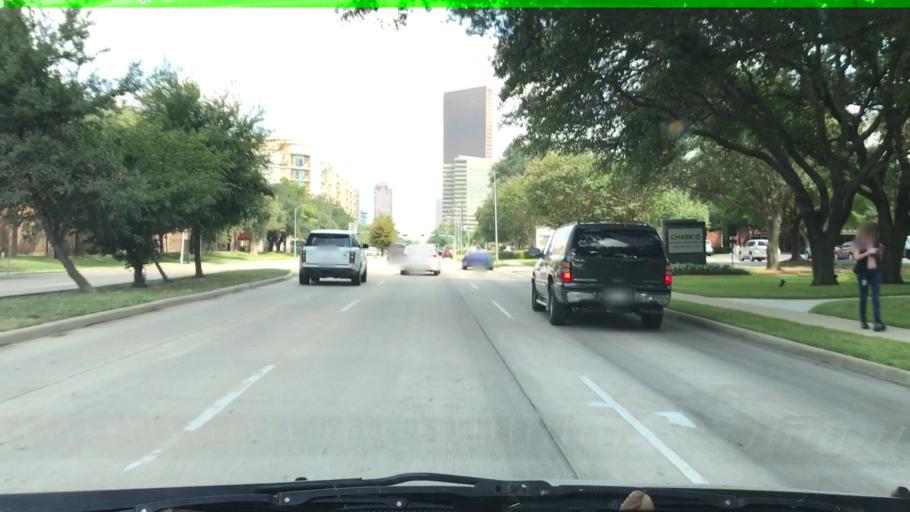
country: US
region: Texas
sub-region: Harris County
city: Hunters Creek Village
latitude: 29.7499
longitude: -95.4817
